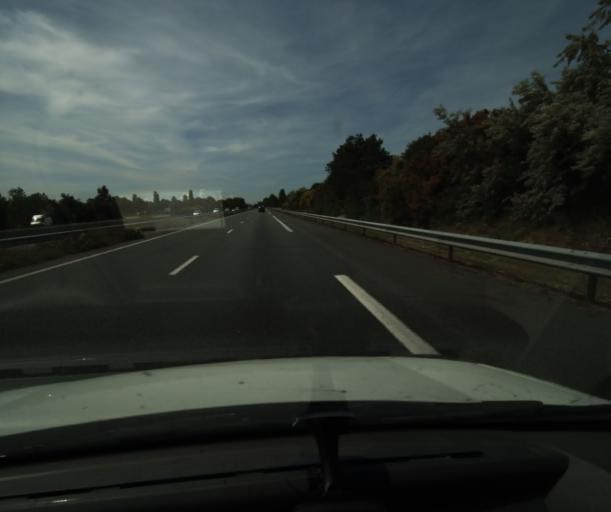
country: FR
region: Languedoc-Roussillon
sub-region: Departement de l'Aude
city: Saint-Martin-Lalande
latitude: 43.2762
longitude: 1.9930
